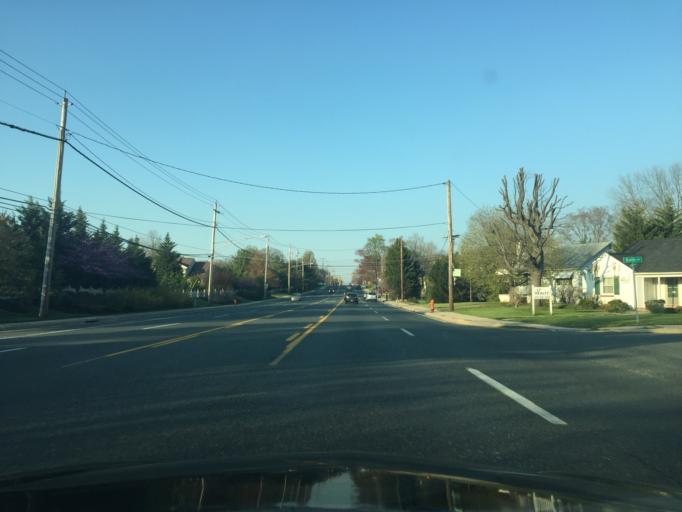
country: US
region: Maryland
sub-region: Baltimore County
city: Perry Hall
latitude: 39.4023
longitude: -76.4761
